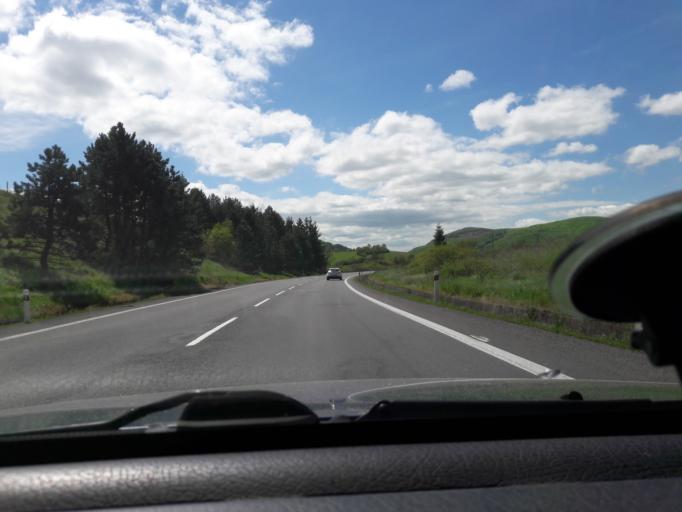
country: SK
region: Banskobystricky
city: Krupina
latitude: 48.4316
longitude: 19.0953
